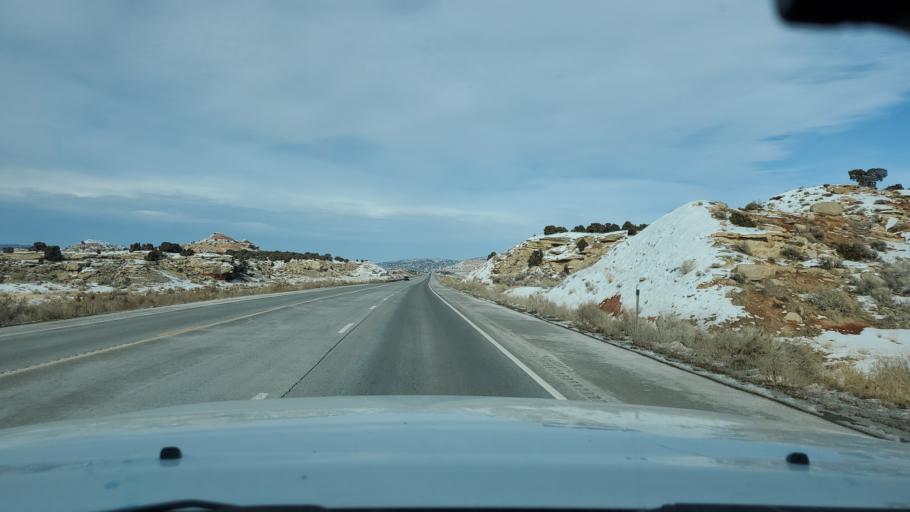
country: US
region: Utah
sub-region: Uintah County
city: Maeser
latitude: 40.3754
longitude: -109.6070
